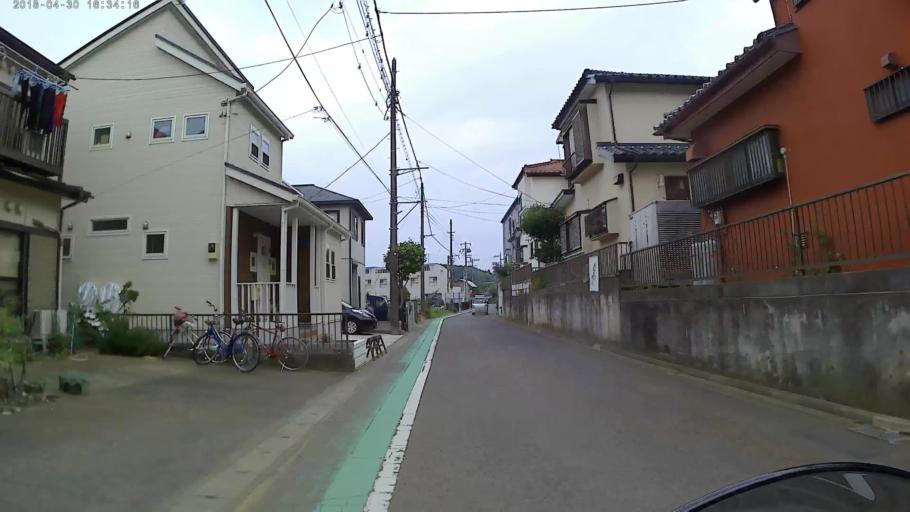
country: JP
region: Kanagawa
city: Zama
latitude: 35.4469
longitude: 139.4075
